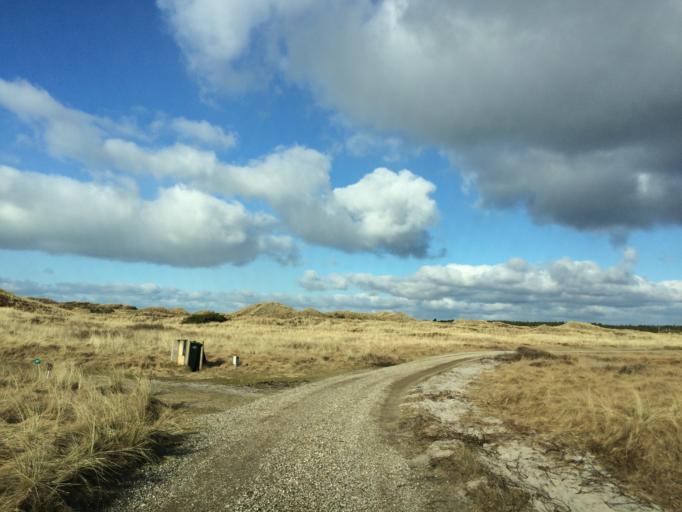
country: DK
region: Central Jutland
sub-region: Holstebro Kommune
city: Ulfborg
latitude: 56.2788
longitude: 8.1344
